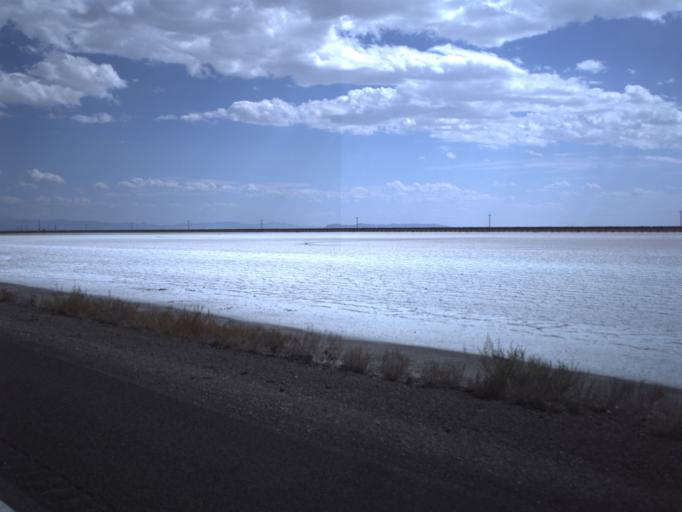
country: US
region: Utah
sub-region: Tooele County
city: Wendover
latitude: 40.7353
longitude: -113.6982
